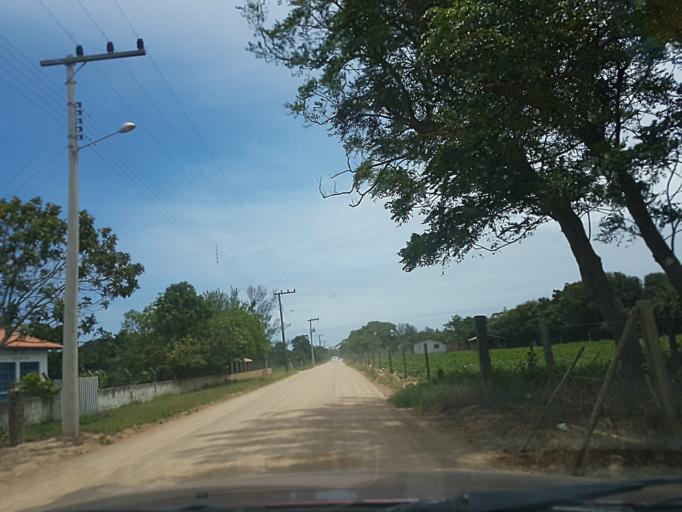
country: BR
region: Santa Catarina
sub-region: Jaguaruna
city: Jaguaruna
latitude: -28.6427
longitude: -48.9647
